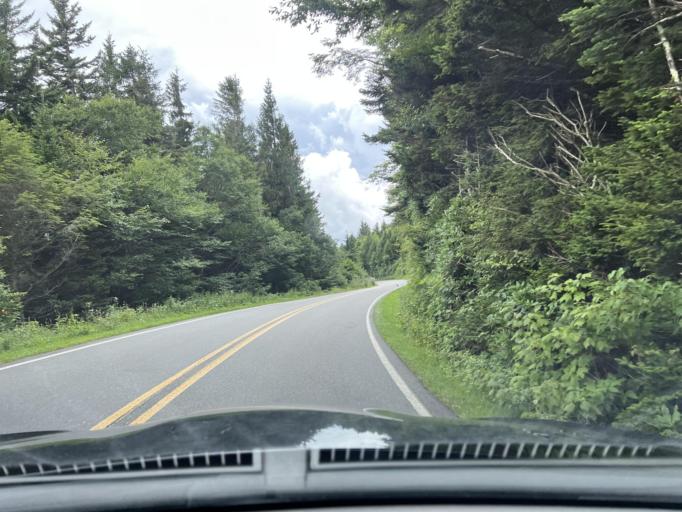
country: US
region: North Carolina
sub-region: Buncombe County
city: Black Mountain
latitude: 35.7323
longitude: -82.2792
